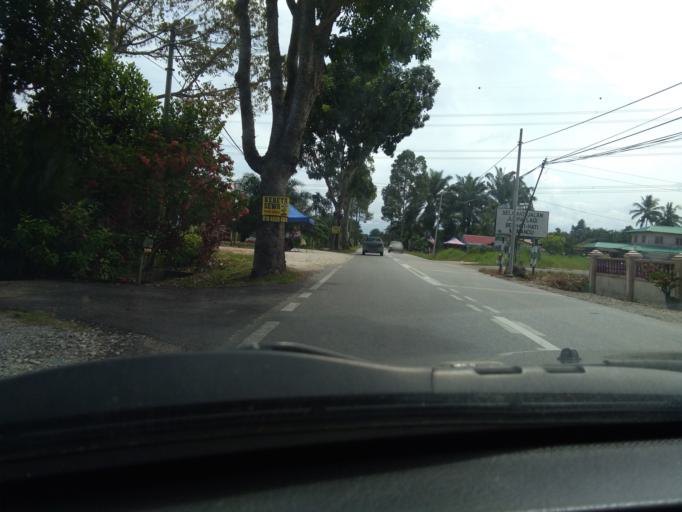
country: MY
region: Perak
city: Bagan Serai
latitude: 5.0527
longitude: 100.5895
